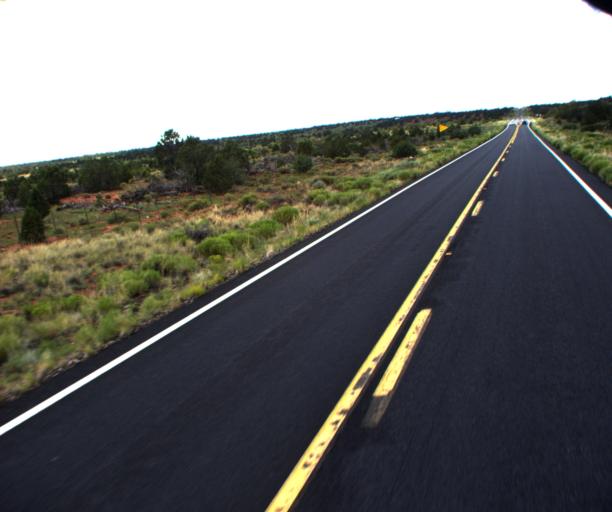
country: US
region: Arizona
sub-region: Coconino County
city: Parks
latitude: 35.6031
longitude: -112.0353
